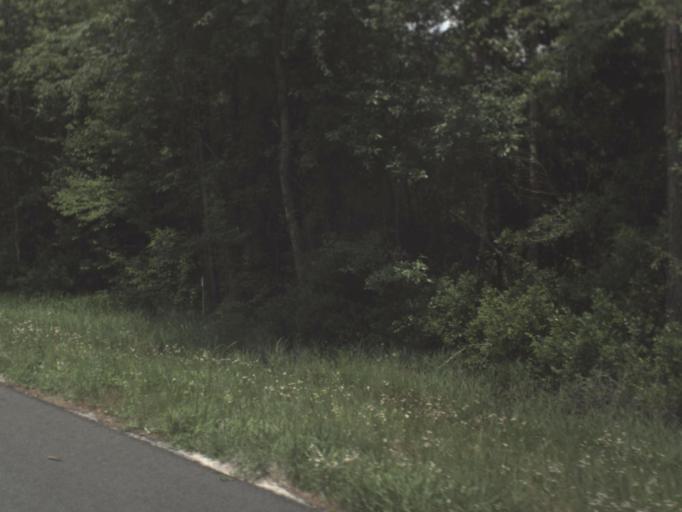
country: US
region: Florida
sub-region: Columbia County
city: Five Points
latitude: 30.3928
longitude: -82.6293
